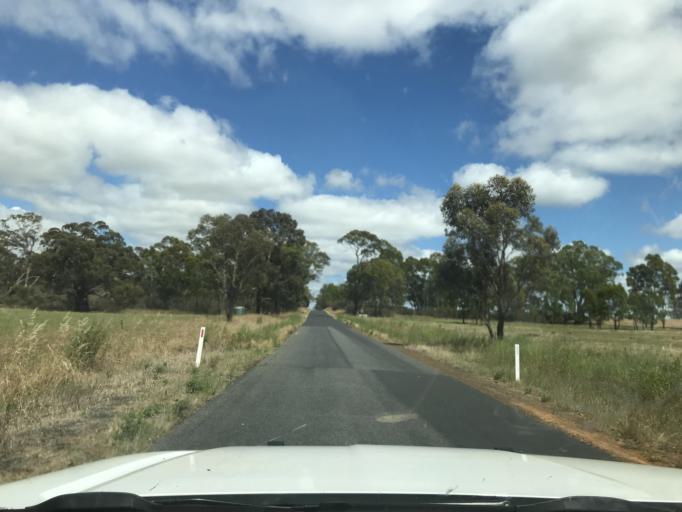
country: AU
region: South Australia
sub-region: Naracoorte and Lucindale
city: Naracoorte
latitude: -36.6827
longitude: 141.3062
